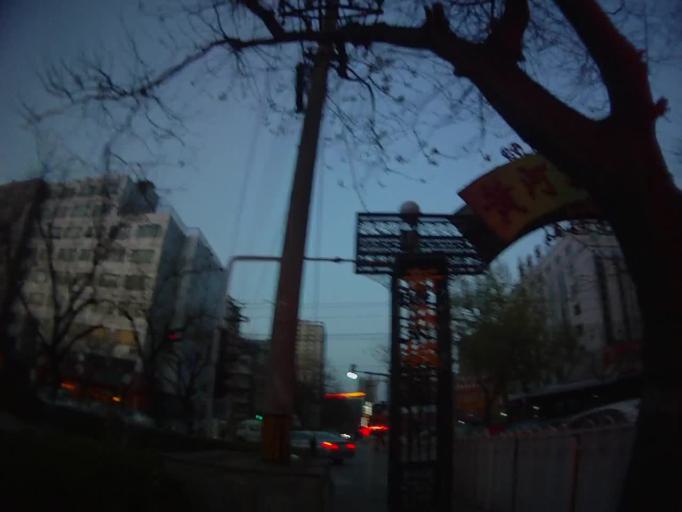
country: CN
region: Beijing
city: Longtan
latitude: 39.8879
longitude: 116.4337
